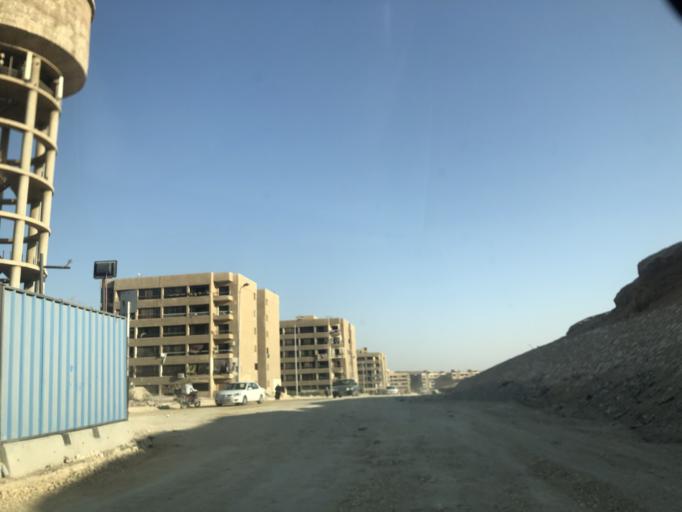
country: EG
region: Al Jizah
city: Al Jizah
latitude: 29.9901
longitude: 31.1110
